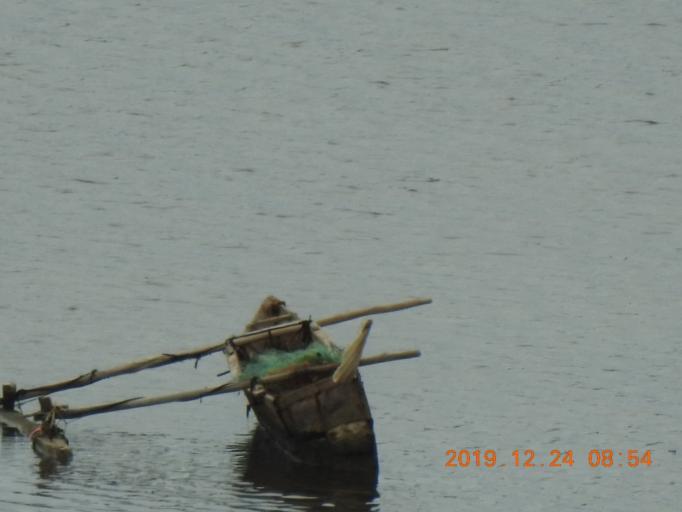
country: MG
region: Diana
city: Antsiranana
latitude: -12.2994
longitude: 49.2988
